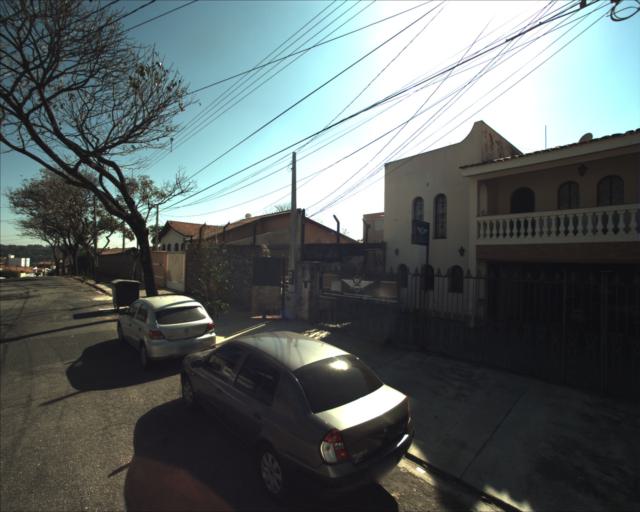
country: BR
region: Sao Paulo
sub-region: Sorocaba
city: Sorocaba
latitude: -23.5111
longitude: -47.4289
